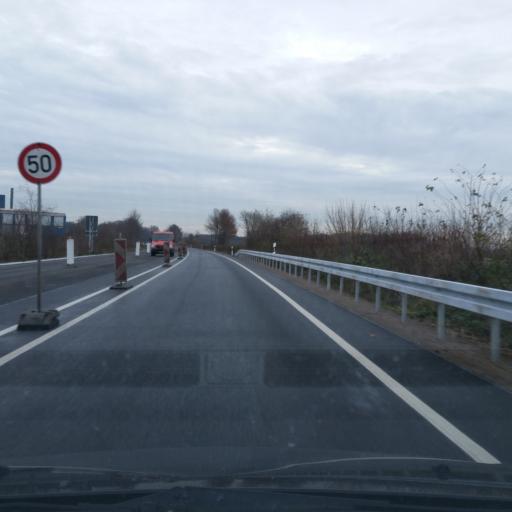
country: DE
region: North Rhine-Westphalia
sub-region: Regierungsbezirk Dusseldorf
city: Mehrhoog
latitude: 51.8073
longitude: 6.5441
